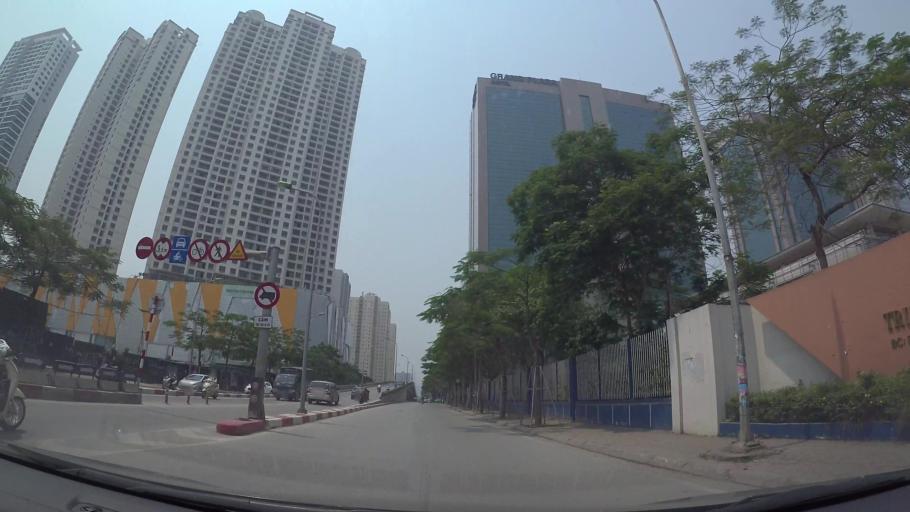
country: VN
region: Ha Noi
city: Thanh Xuan
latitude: 21.0061
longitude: 105.7972
